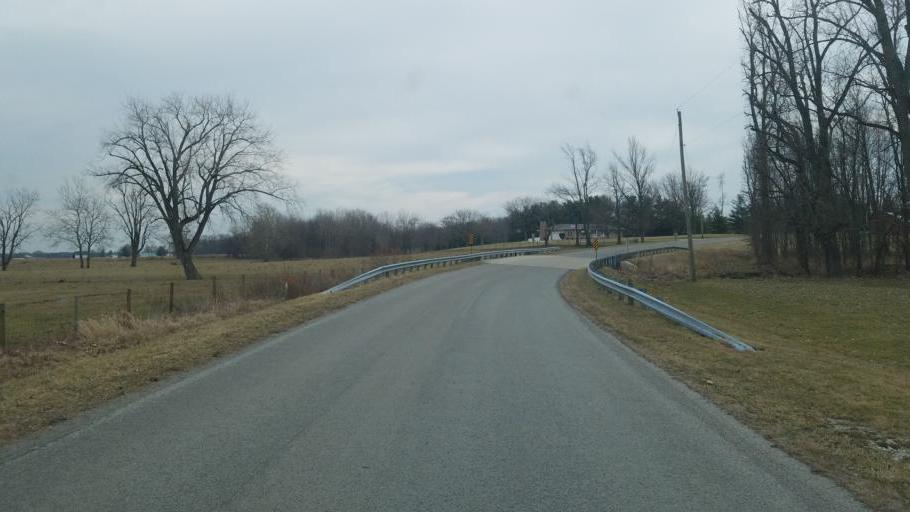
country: US
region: Ohio
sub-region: Richland County
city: Shelby
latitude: 40.8346
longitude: -82.6439
